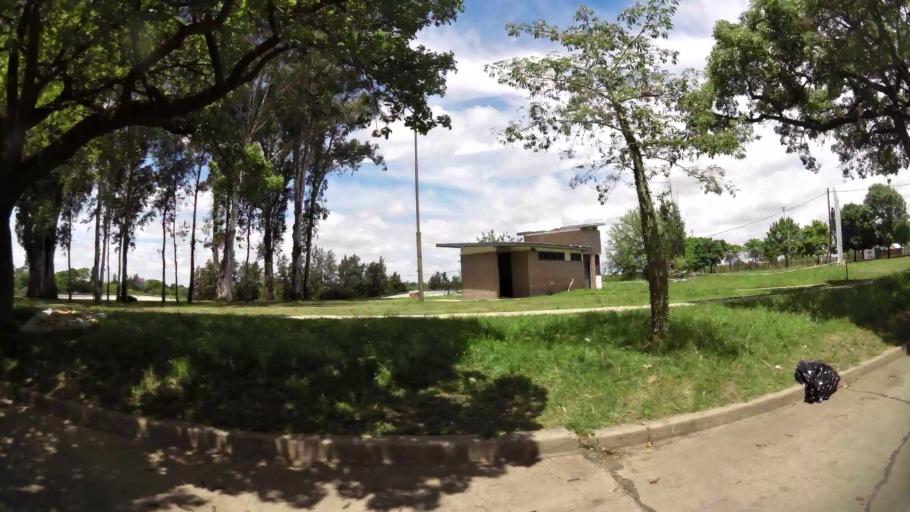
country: AR
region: Santa Fe
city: Gobernador Galvez
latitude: -33.0022
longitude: -60.6224
